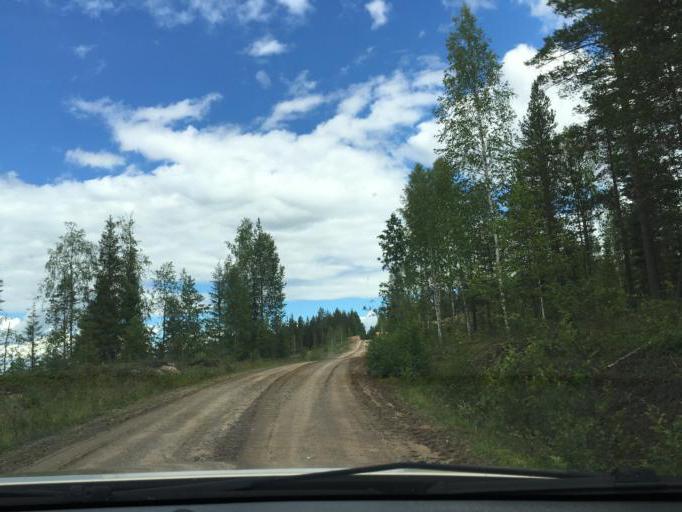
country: SE
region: Norrbotten
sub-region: Overkalix Kommun
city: OEverkalix
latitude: 66.1447
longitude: 22.7885
